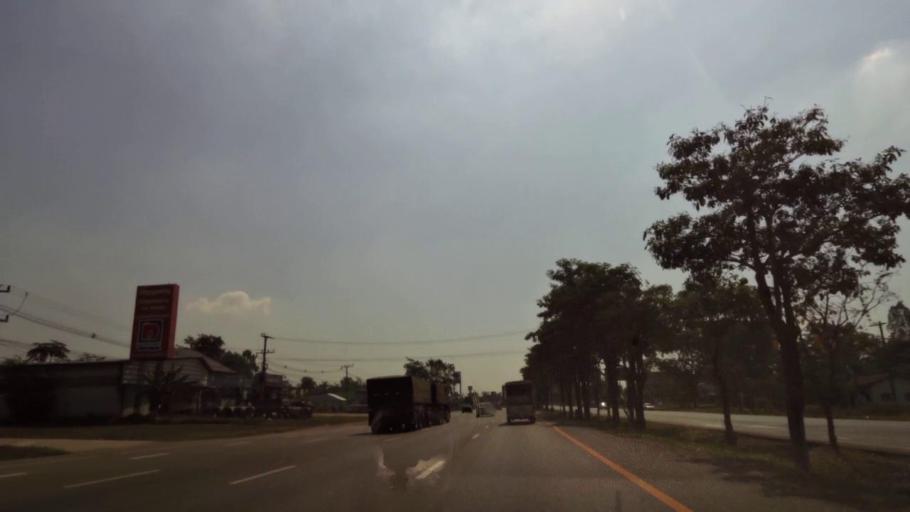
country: TH
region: Phichit
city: Bueng Na Rang
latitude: 16.1218
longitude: 100.1257
